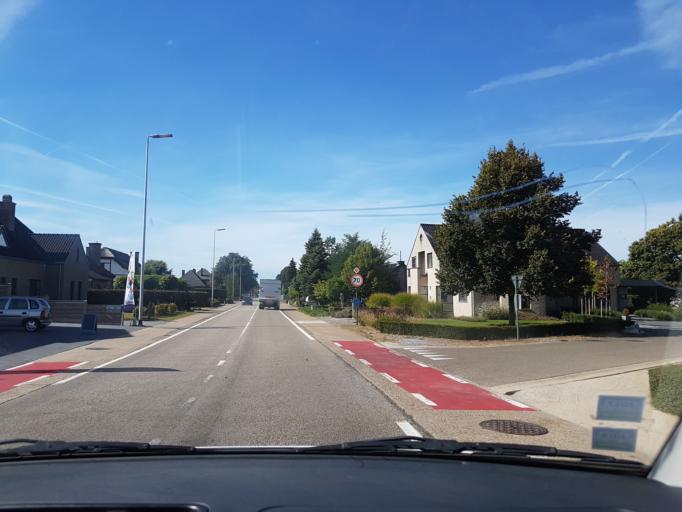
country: BE
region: Flanders
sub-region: Provincie Limburg
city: Overpelt
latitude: 51.2099
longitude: 5.4147
